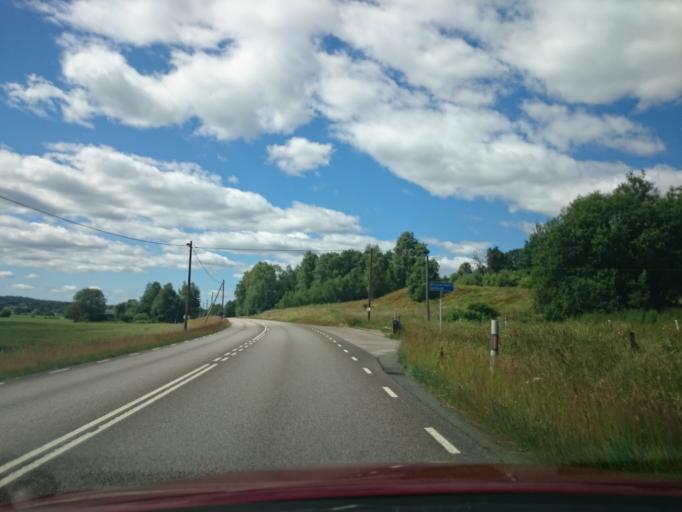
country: SE
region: Vaestra Goetaland
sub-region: Lerums Kommun
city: Olstorp
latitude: 57.8190
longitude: 12.2000
